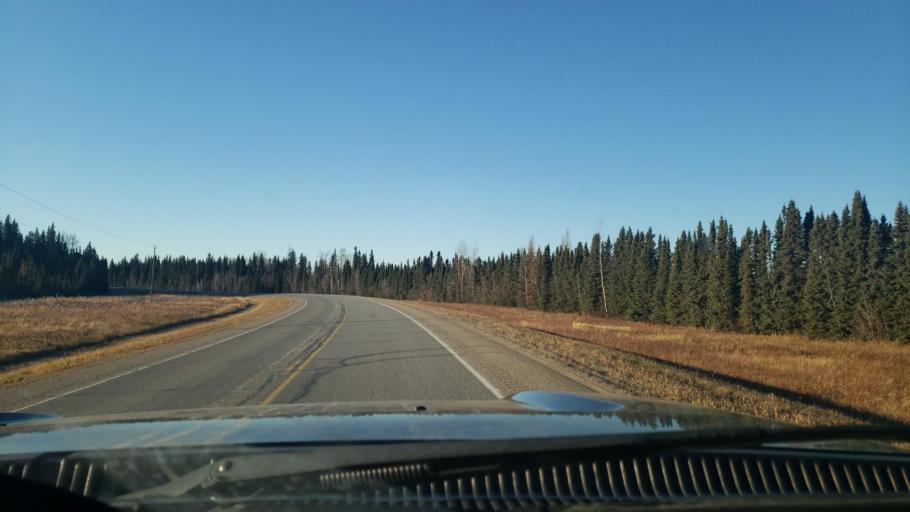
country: CA
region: British Columbia
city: Fort Nelson
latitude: 58.1279
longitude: -122.7166
